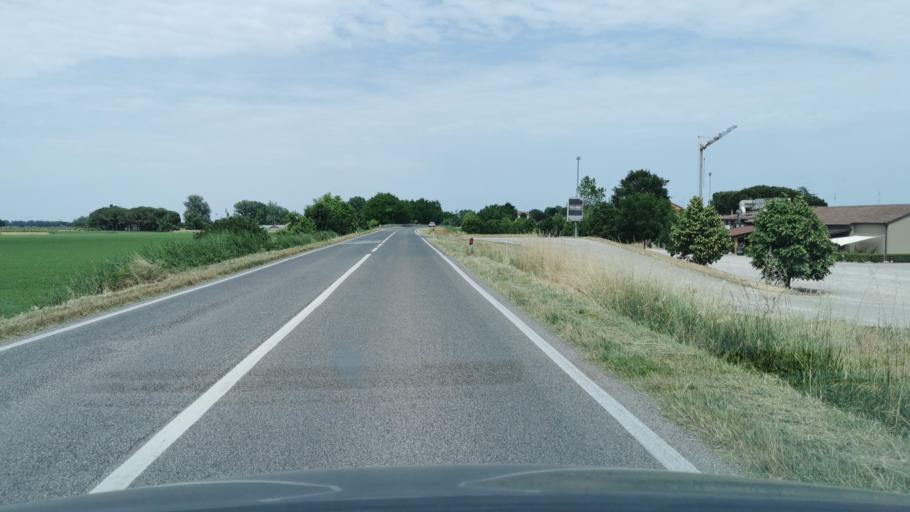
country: IT
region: Emilia-Romagna
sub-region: Provincia di Ravenna
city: Savarna-Conventella
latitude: 44.5125
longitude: 12.1014
